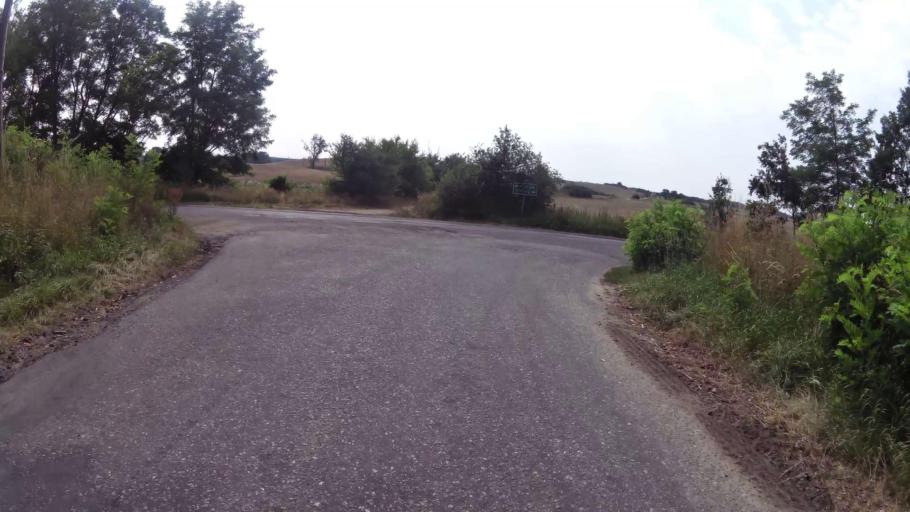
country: PL
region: West Pomeranian Voivodeship
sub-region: Powiat gryfinski
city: Mieszkowice
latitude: 52.8709
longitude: 14.5215
